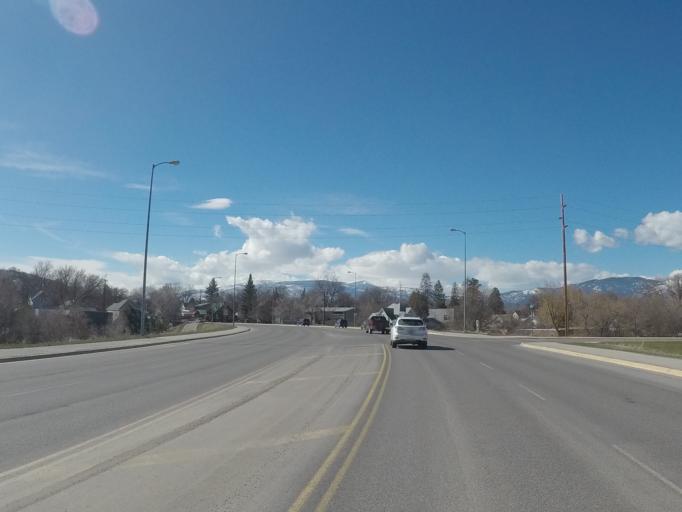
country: US
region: Montana
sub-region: Missoula County
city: Missoula
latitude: 46.8708
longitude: -114.0022
